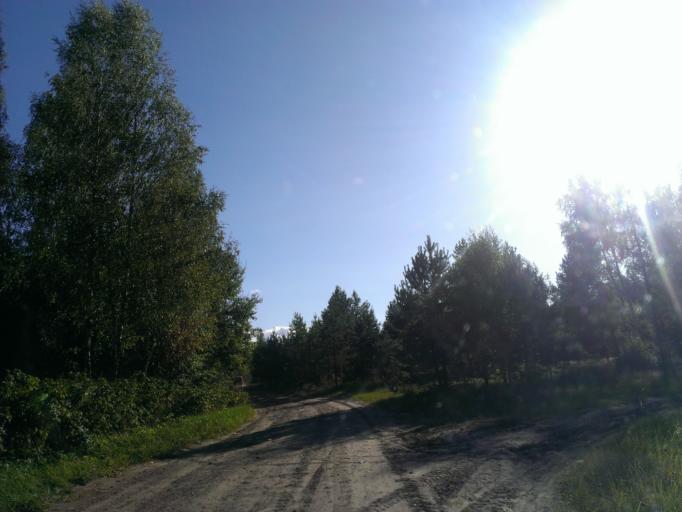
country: LV
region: Adazi
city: Adazi
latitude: 57.0589
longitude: 24.2587
